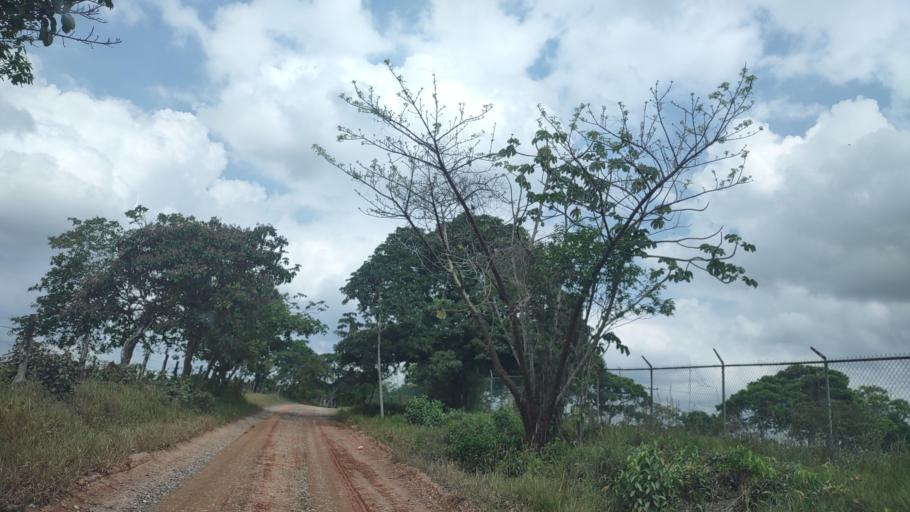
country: MX
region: Veracruz
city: Las Choapas
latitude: 17.9574
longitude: -94.1142
